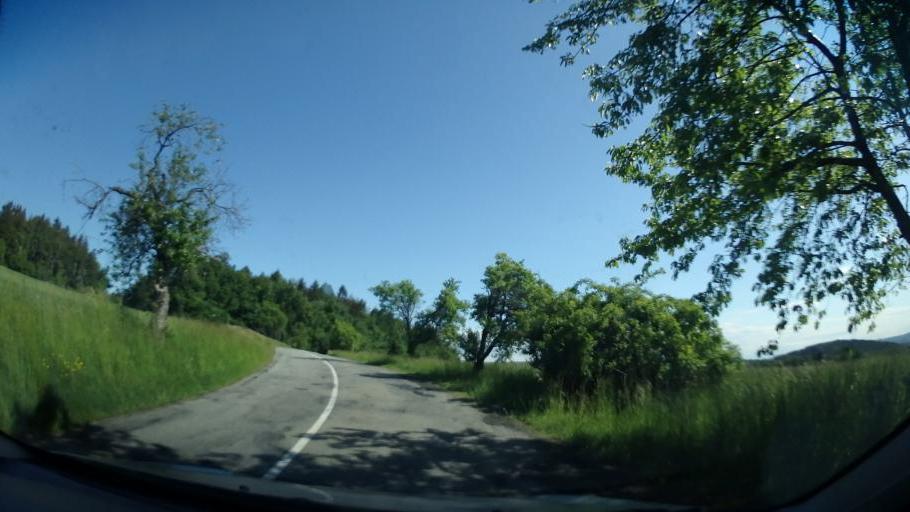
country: CZ
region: South Moravian
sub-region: Okres Blansko
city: Letovice
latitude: 49.6019
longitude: 16.6068
